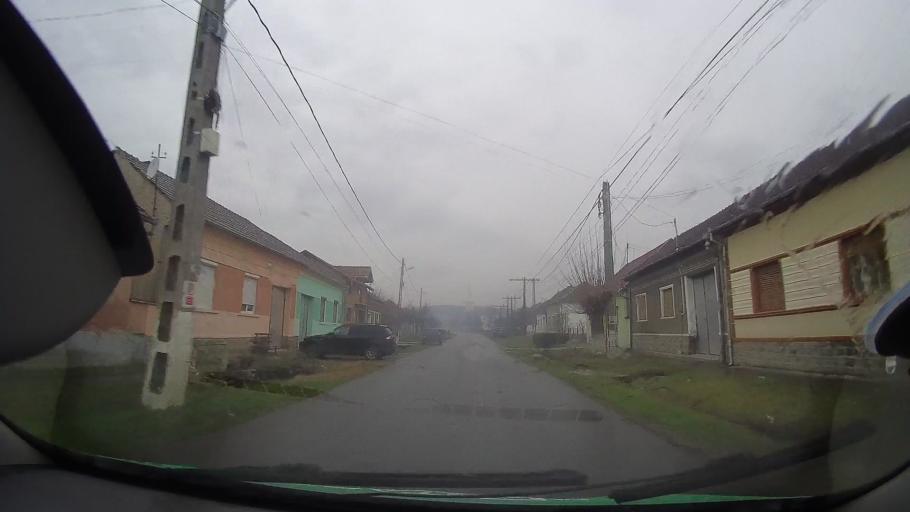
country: RO
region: Bihor
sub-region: Comuna Uileacu de Beius
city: Uileacu de Beius
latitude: 46.6832
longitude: 22.2230
